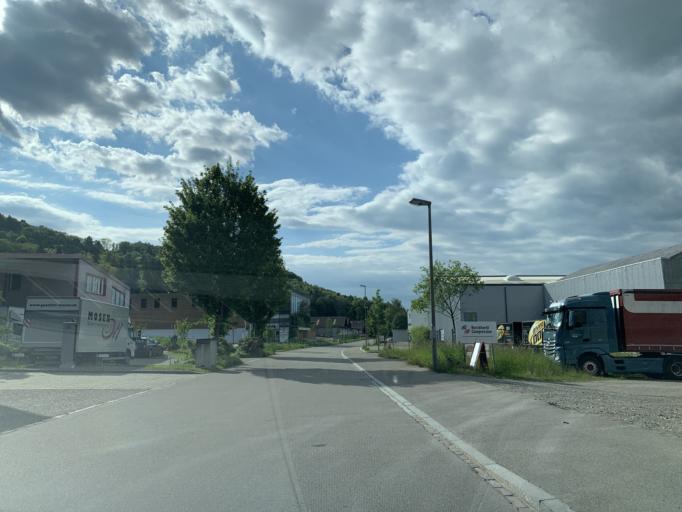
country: CH
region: Zurich
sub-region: Bezirk Winterthur
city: Wuelflingen (Kreis 6) / Niederfeld
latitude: 47.5070
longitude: 8.6766
